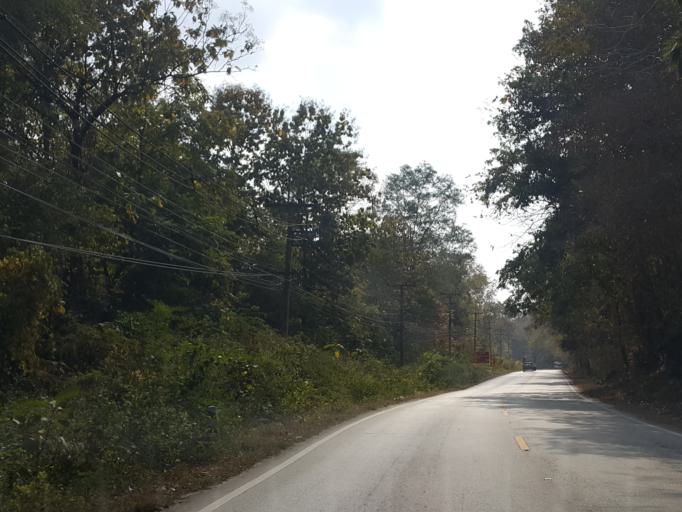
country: TH
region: Chiang Mai
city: Hot
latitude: 18.2132
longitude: 98.4464
